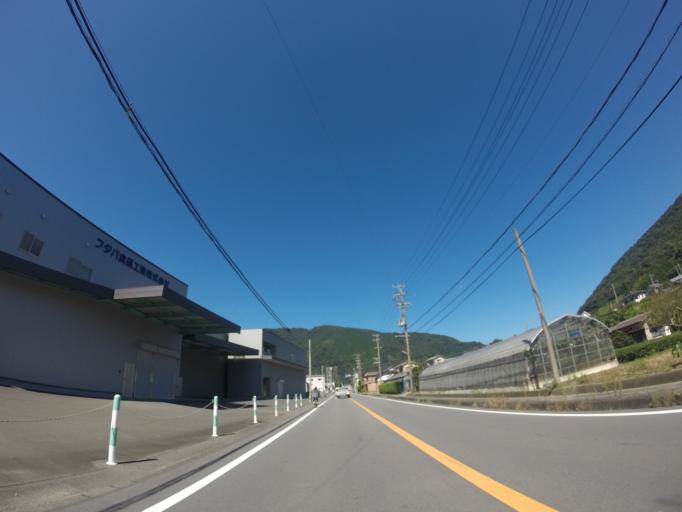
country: JP
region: Shizuoka
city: Kanaya
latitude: 34.8730
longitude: 138.1130
